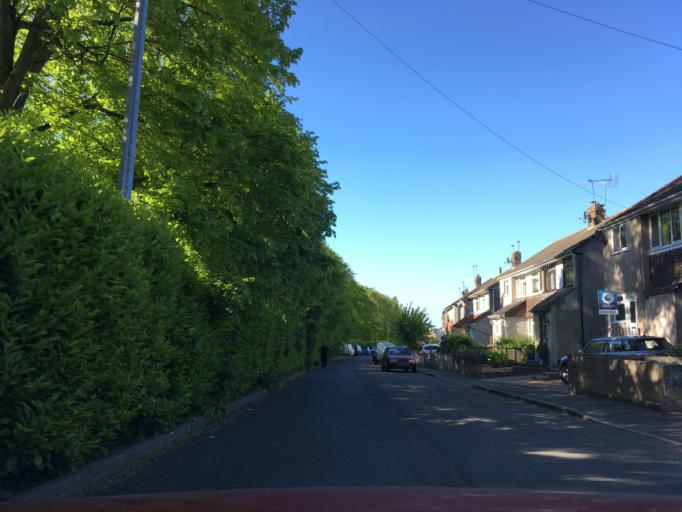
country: GB
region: England
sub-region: North Somerset
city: Portishead
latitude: 51.4924
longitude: -2.7636
